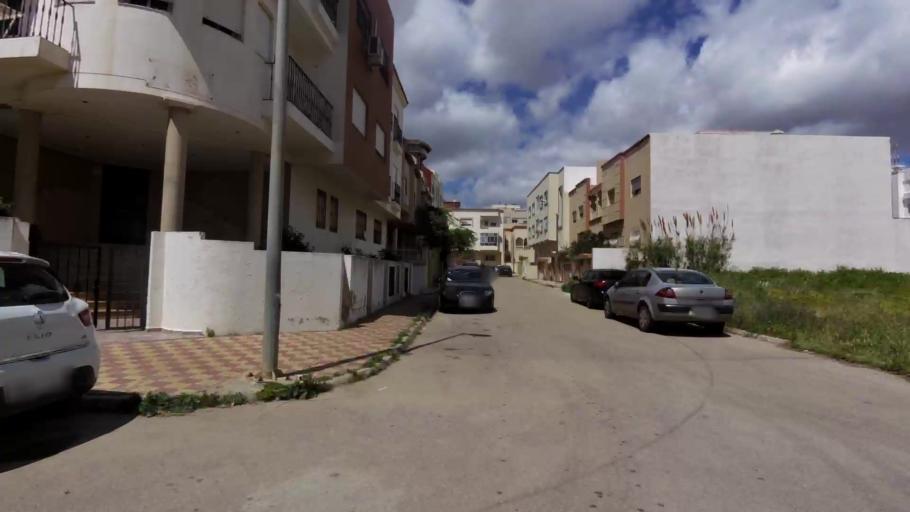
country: MA
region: Tanger-Tetouan
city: Tetouan
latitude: 35.5744
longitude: -5.3425
